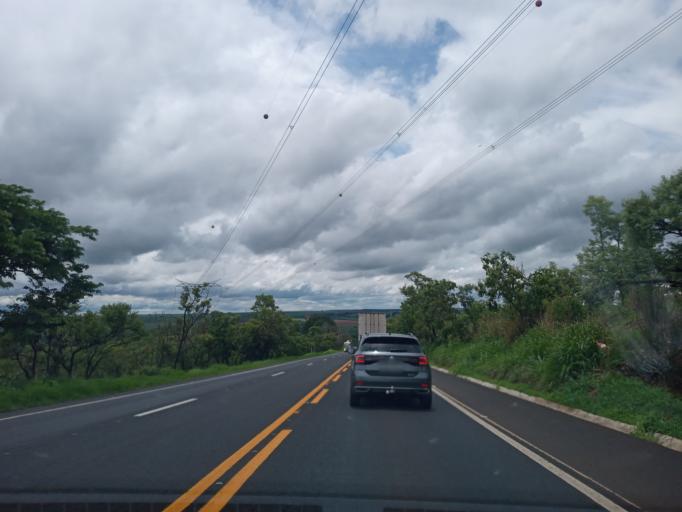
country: BR
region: Minas Gerais
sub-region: Uberaba
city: Uberaba
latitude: -19.2884
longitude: -47.6142
